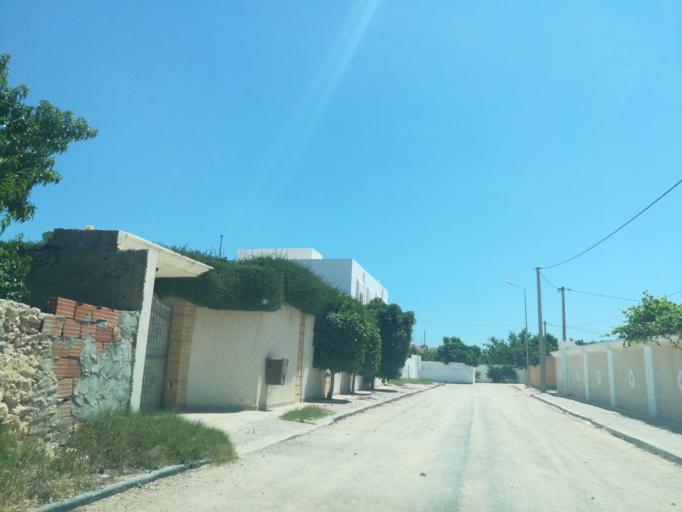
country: TN
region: Safaqis
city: Al Qarmadah
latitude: 34.8145
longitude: 10.7601
